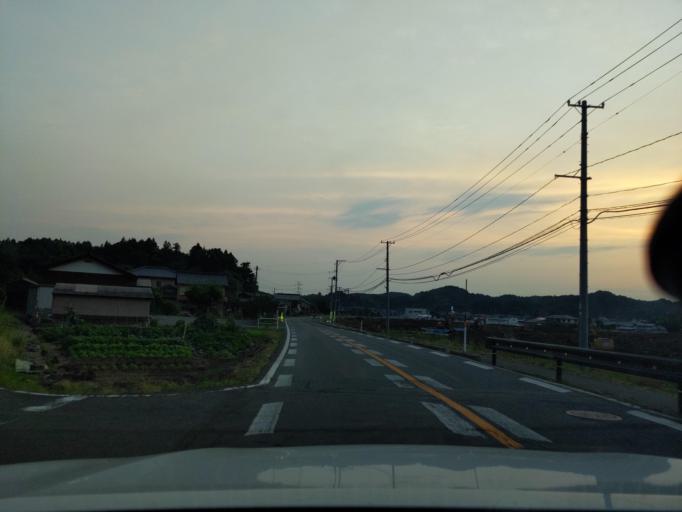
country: JP
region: Niigata
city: Kashiwazaki
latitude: 37.4463
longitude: 138.6459
